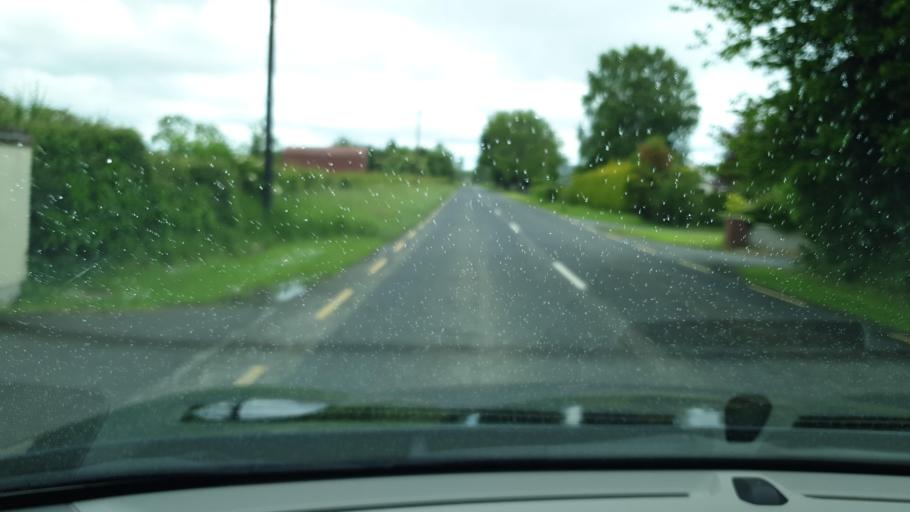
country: IE
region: Leinster
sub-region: An Mhi
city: Dunboyne
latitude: 53.4305
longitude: -6.5081
